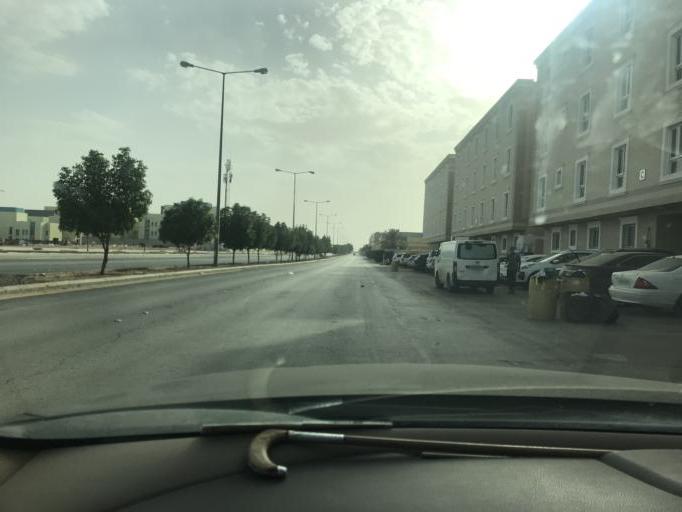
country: SA
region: Ar Riyad
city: Riyadh
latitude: 24.7809
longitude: 46.7157
